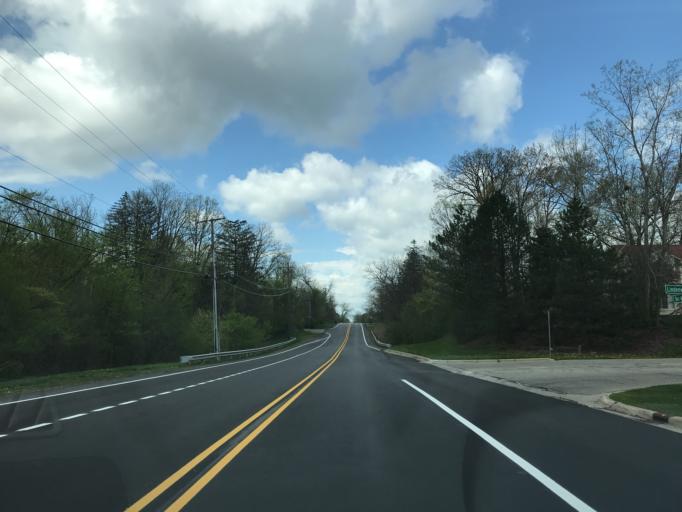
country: US
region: Michigan
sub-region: Oakland County
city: Franklin
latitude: 42.4713
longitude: -83.3072
